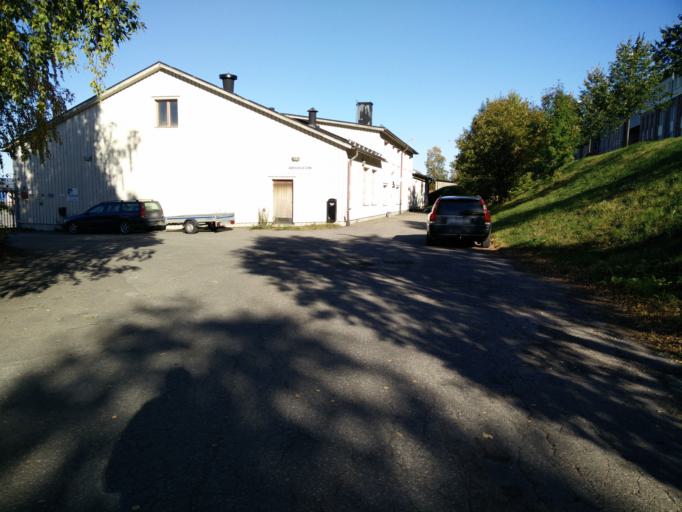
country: SE
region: Vaesternorrland
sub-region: Haernoesands Kommun
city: Haernoesand
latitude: 62.6396
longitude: 17.9507
